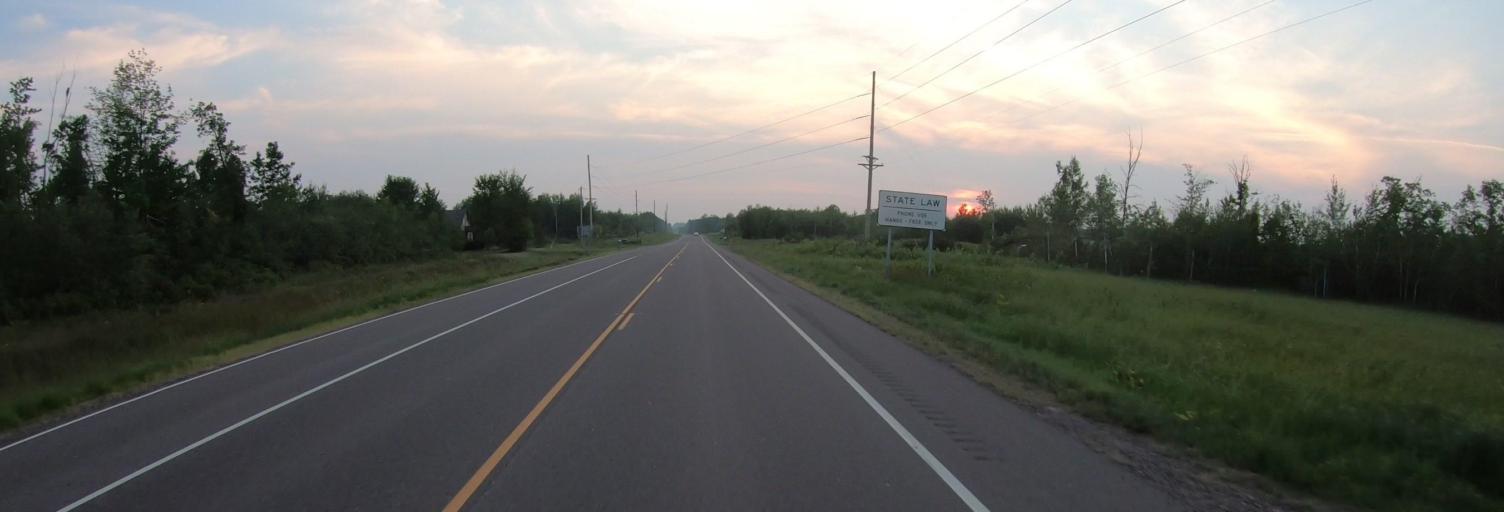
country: US
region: Wisconsin
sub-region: Burnett County
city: Grantsburg
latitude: 45.7735
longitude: -92.7896
